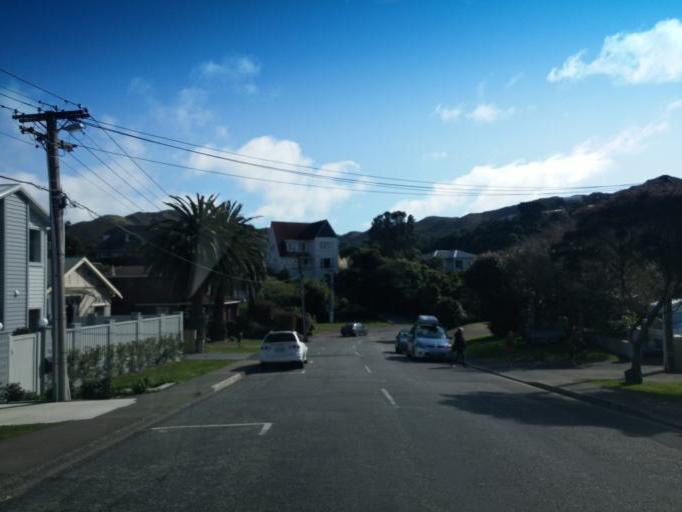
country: NZ
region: Wellington
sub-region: Wellington City
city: Kelburn
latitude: -41.2484
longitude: 174.7825
